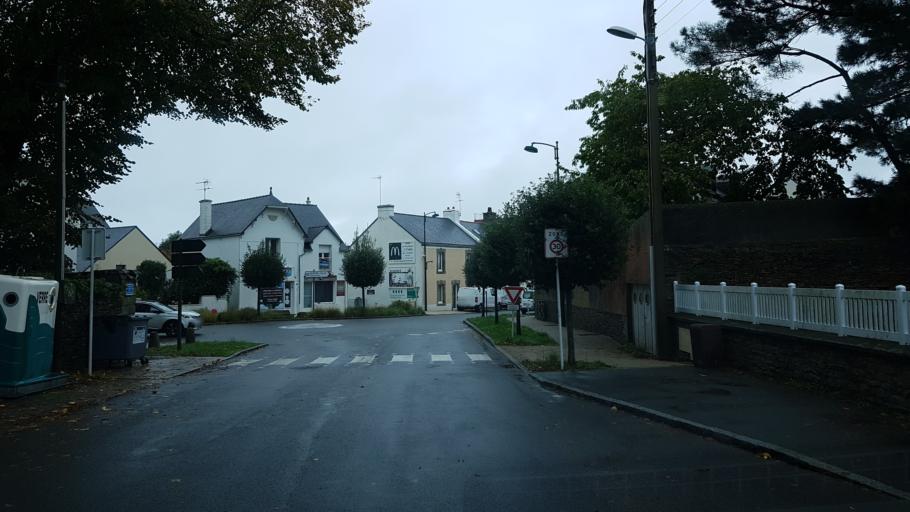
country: FR
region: Brittany
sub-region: Departement du Morbihan
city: Sarzeau
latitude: 47.5258
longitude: -2.7732
